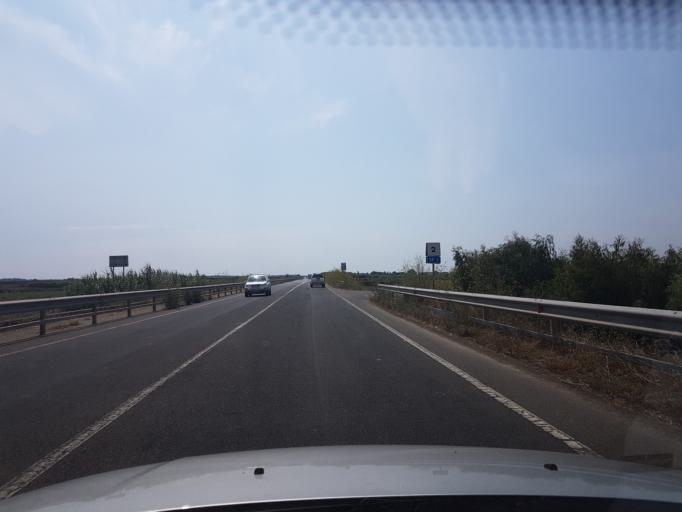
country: IT
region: Sardinia
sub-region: Provincia di Oristano
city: Solanas
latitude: 39.9191
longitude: 8.5584
